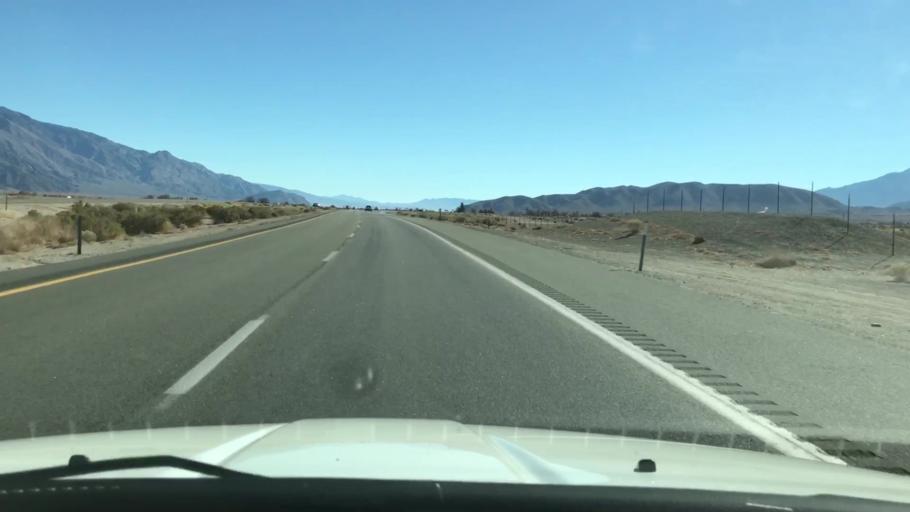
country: US
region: California
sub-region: Inyo County
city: Lone Pine
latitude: 36.7407
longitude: -118.1554
